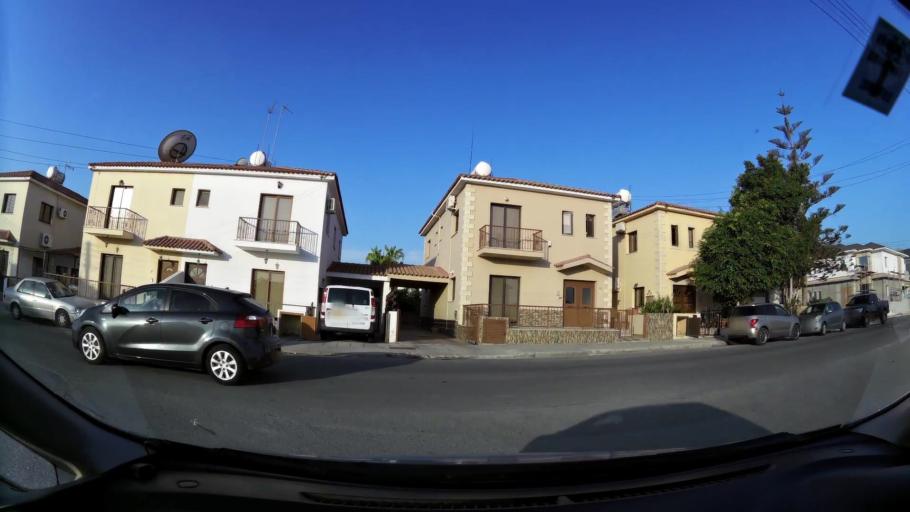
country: CY
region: Larnaka
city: Aradippou
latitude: 34.9283
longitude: 33.5921
